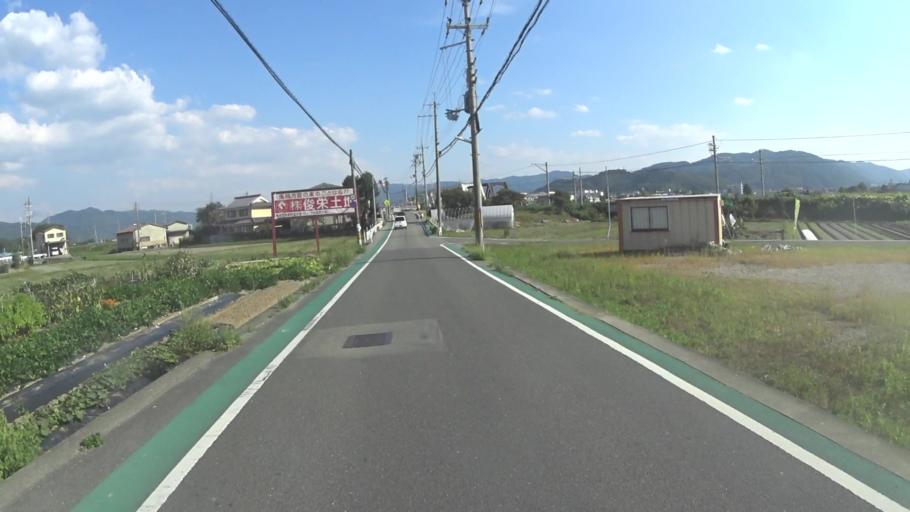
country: JP
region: Kyoto
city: Kameoka
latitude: 35.0275
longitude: 135.5602
